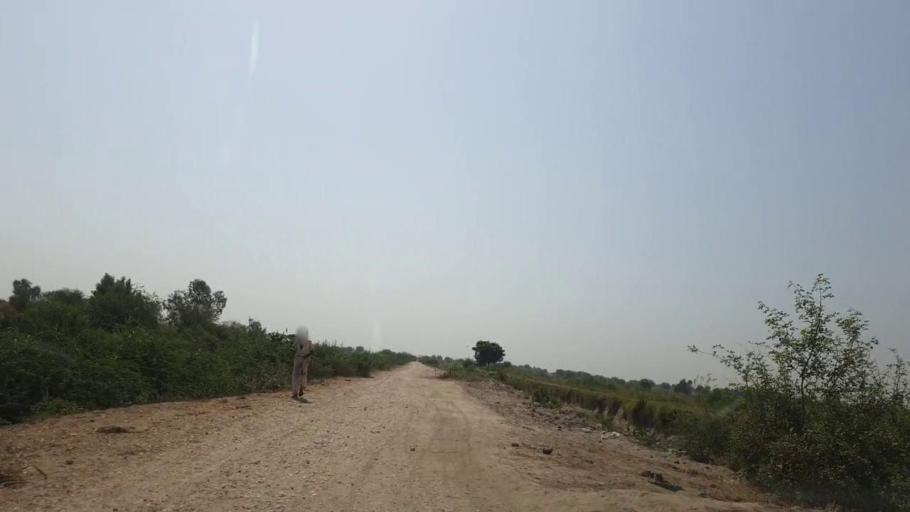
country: PK
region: Sindh
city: Jhol
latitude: 25.8817
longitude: 69.0372
